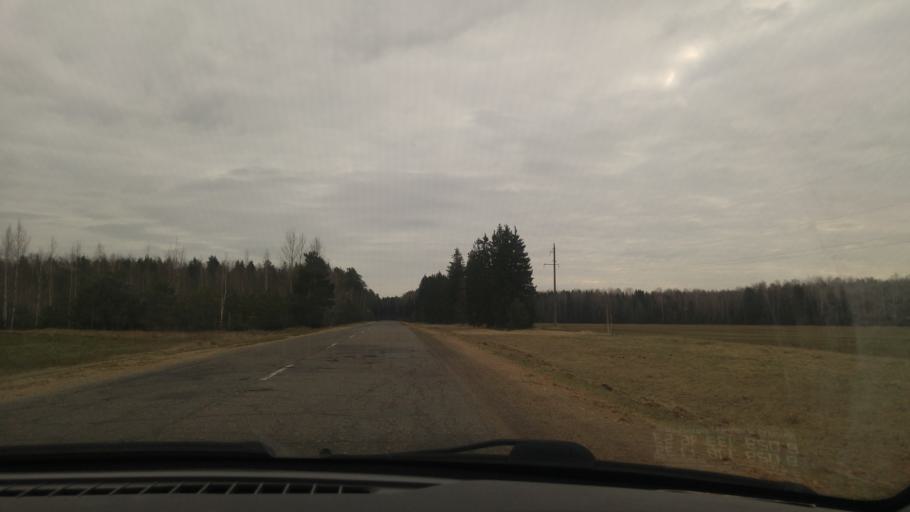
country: BY
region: Minsk
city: Pukhavichy
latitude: 53.7064
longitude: 28.2389
